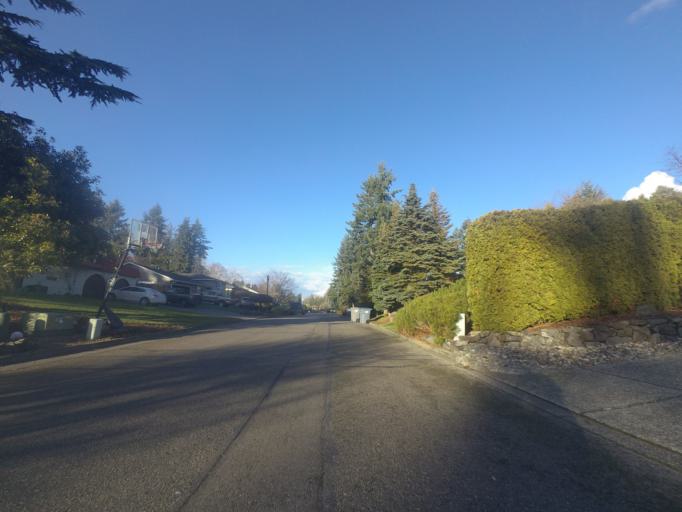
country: US
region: Washington
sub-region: Pierce County
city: Fircrest
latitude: 47.2226
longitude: -122.5205
